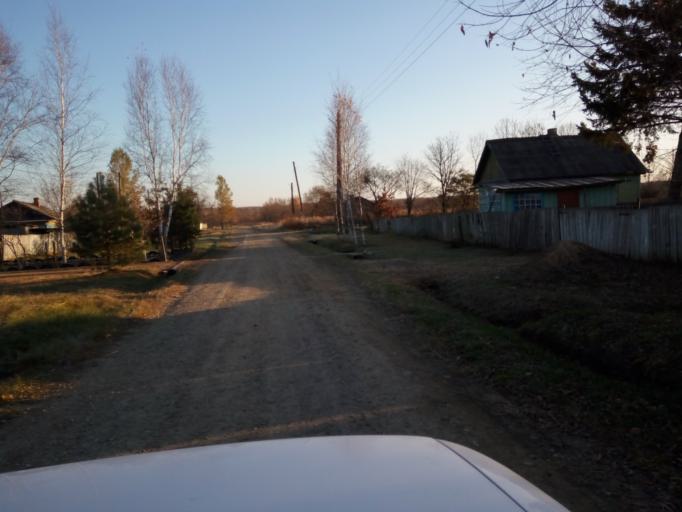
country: RU
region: Primorskiy
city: Lazo
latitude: 45.8809
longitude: 133.6538
